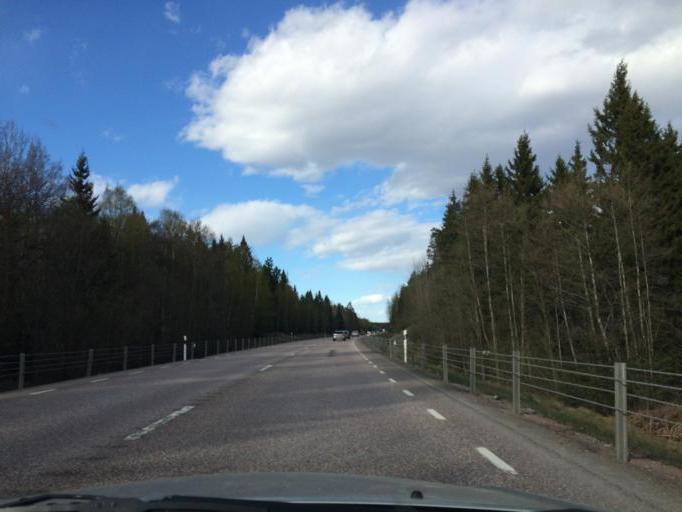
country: SE
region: Soedermanland
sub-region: Eskilstuna Kommun
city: Kvicksund
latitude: 59.5064
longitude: 16.3069
